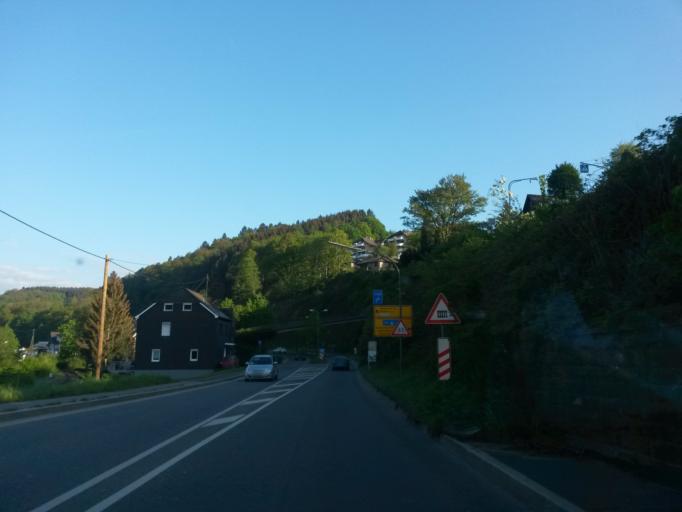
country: DE
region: North Rhine-Westphalia
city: Wiehl
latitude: 50.9625
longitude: 7.5091
